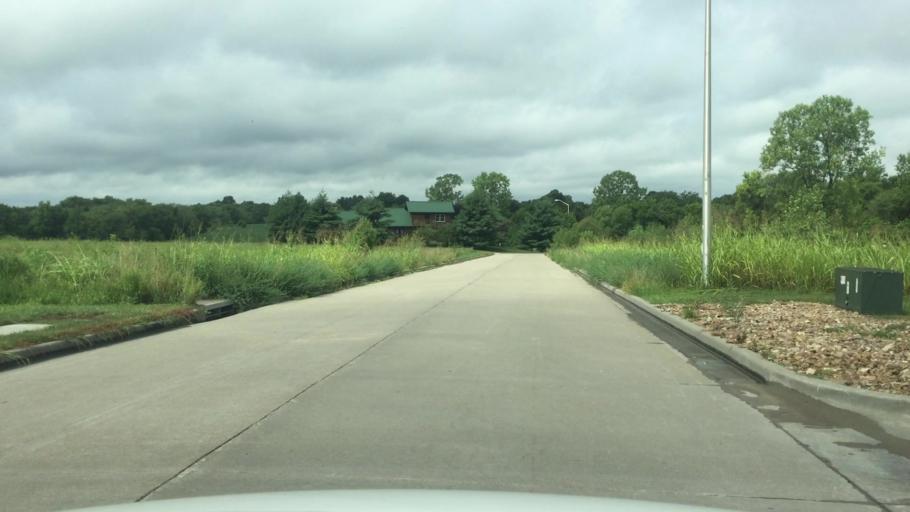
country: US
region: Missouri
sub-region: Jackson County
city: Lone Jack
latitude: 38.8804
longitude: -94.2111
